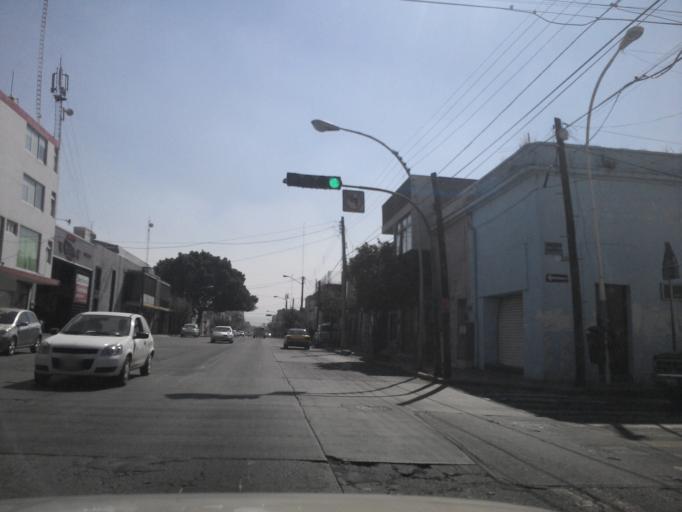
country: MX
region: Jalisco
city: Guadalajara
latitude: 20.6841
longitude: -103.3592
